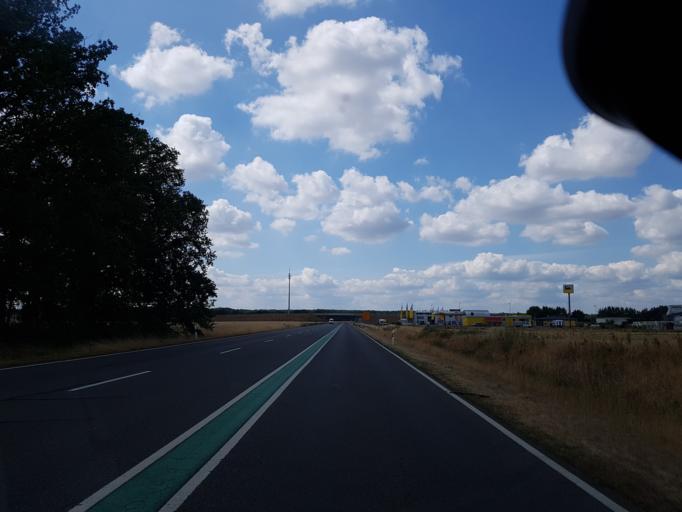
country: DE
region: Brandenburg
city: Drebkau
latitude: 51.6481
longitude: 14.2396
